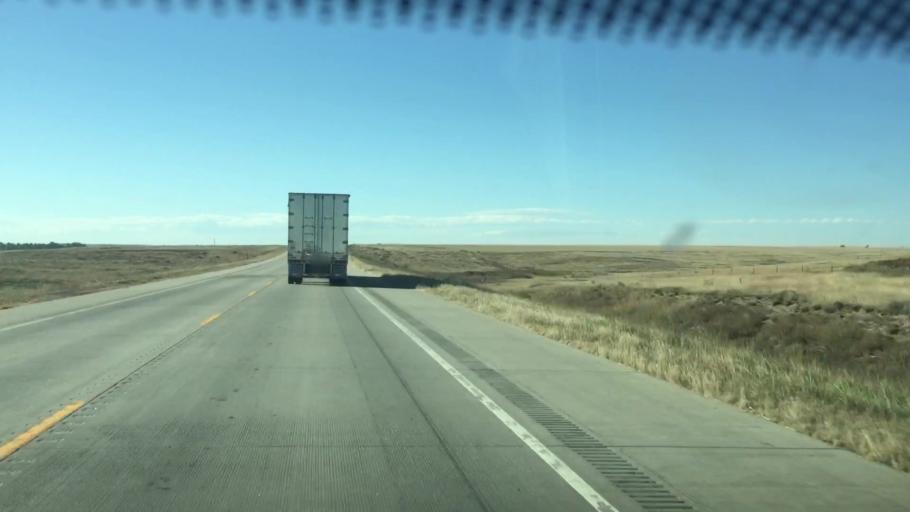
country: US
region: Colorado
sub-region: Kiowa County
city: Eads
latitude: 38.8012
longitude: -102.9584
